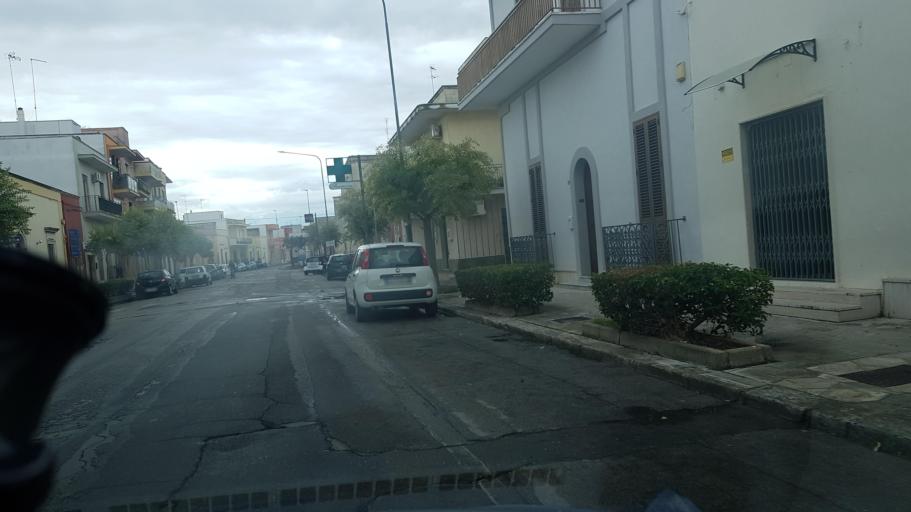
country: IT
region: Apulia
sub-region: Provincia di Lecce
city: Salice Salentino
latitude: 40.3852
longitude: 17.9616
